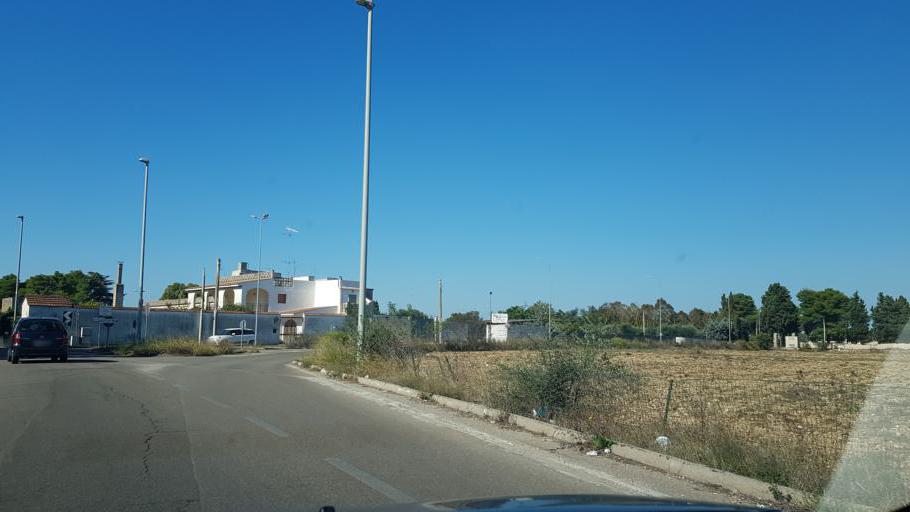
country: IT
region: Apulia
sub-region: Provincia di Lecce
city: Arnesano
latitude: 40.3366
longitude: 18.1085
